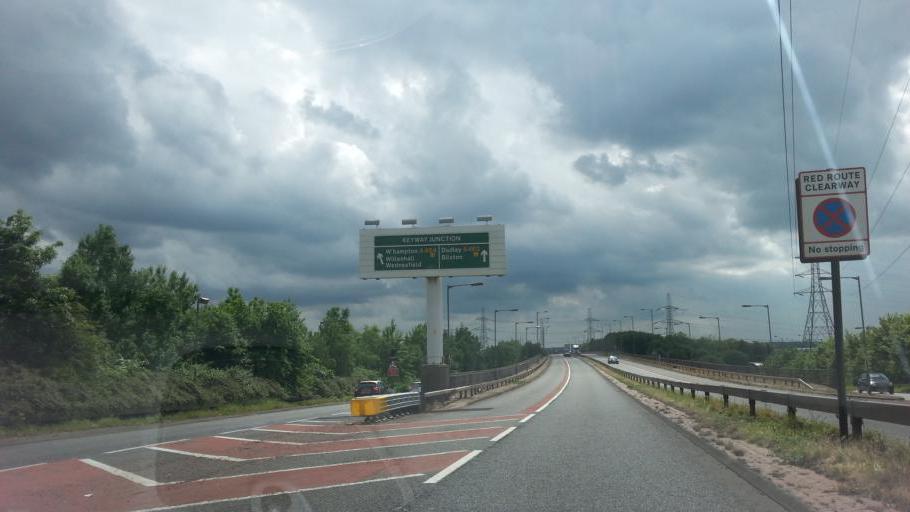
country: GB
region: England
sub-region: Walsall
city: Darlaston
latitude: 52.5770
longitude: -2.0438
